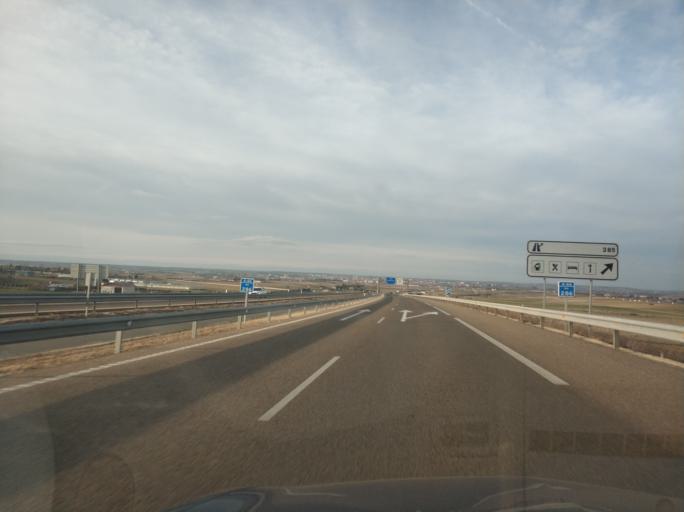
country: ES
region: Castille and Leon
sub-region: Provincia de Zamora
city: Morales del Vino
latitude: 41.4469
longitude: -5.7188
